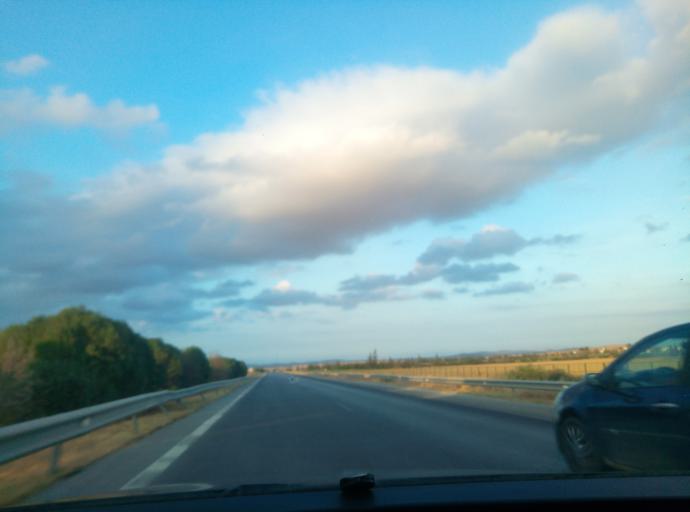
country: TN
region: Manouba
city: El Battan
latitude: 36.6900
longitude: 9.9267
